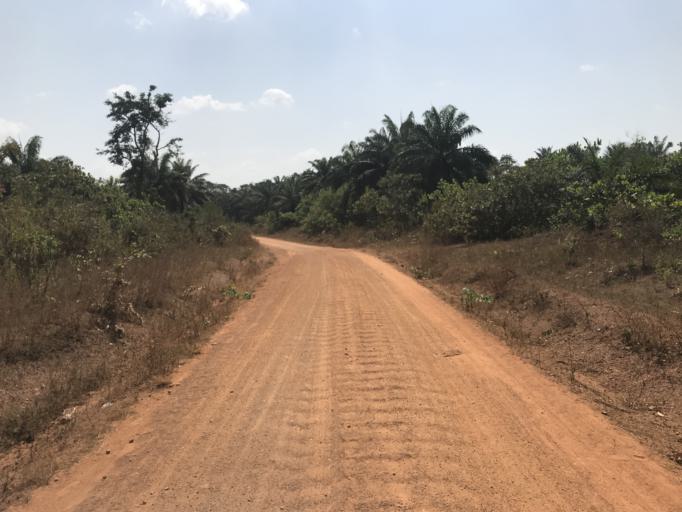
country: NG
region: Osun
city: Ifon
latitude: 7.9078
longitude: 4.4795
